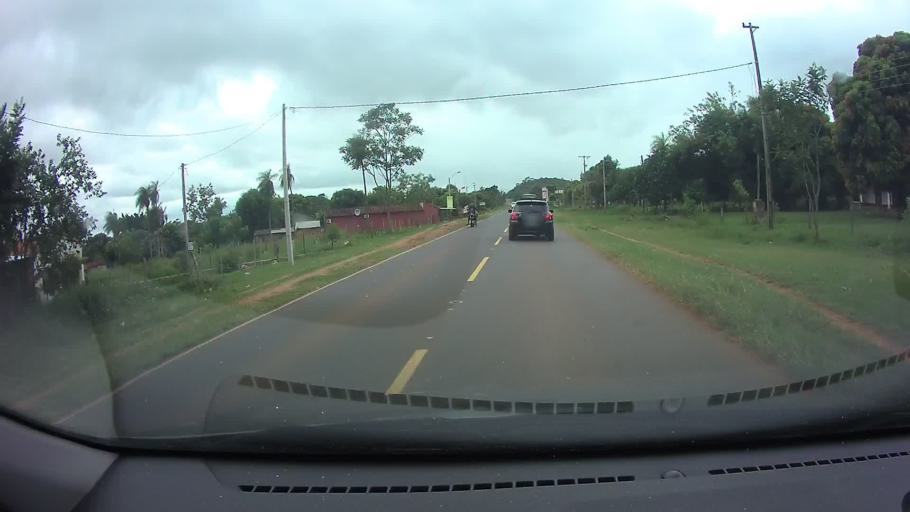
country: PY
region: Paraguari
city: Carapegua
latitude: -25.7412
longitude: -57.2817
